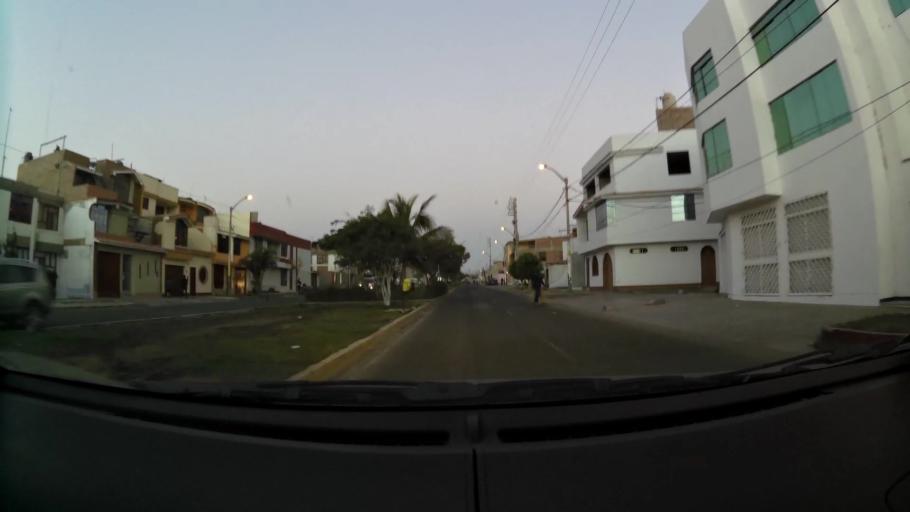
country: PE
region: Ancash
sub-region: Provincia de Santa
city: Buenos Aires
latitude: -9.1229
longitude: -78.5269
